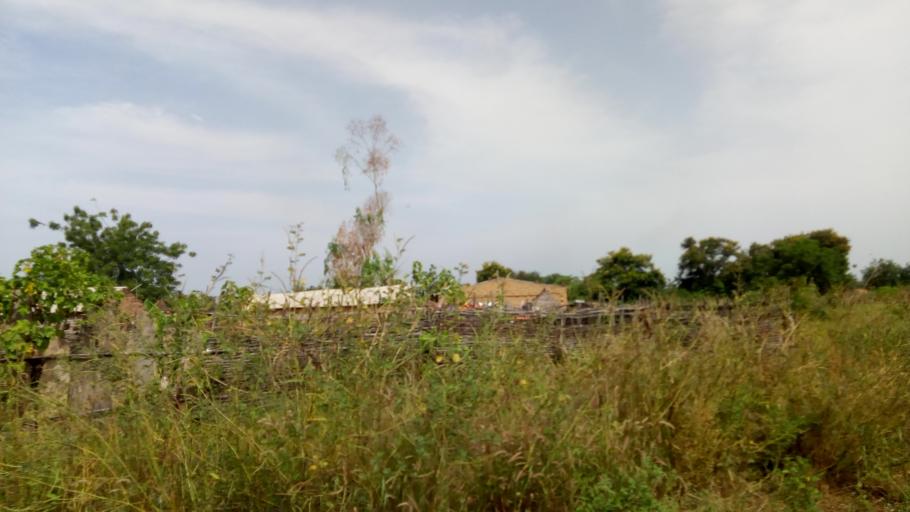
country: ML
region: Kayes
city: Kita
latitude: 13.2622
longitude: -8.8561
